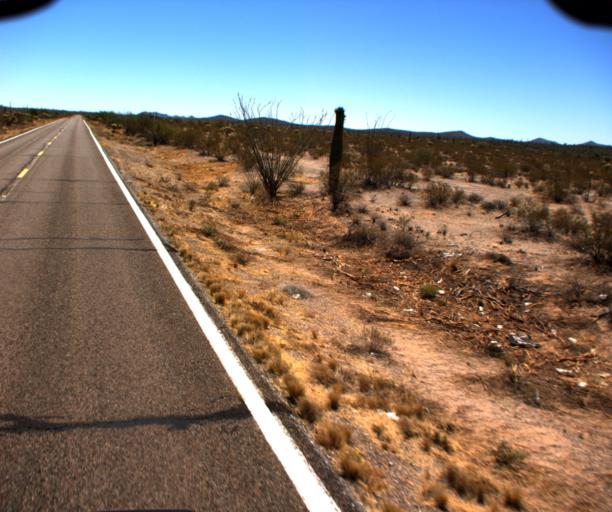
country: US
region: Arizona
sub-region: Pima County
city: Ajo
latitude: 32.2173
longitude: -112.6486
